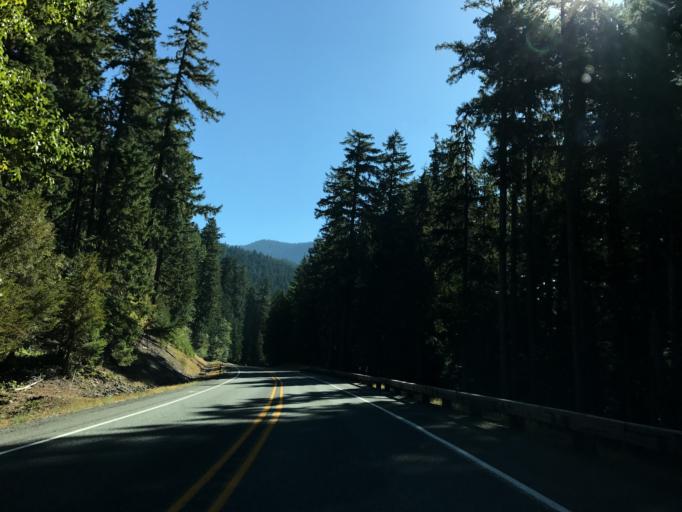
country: US
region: Washington
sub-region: King County
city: Enumclaw
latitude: 47.0293
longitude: -121.5523
